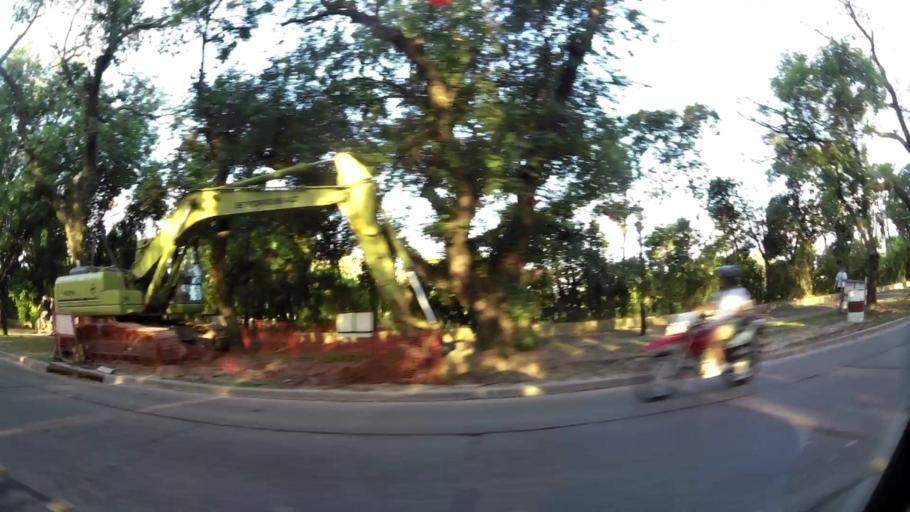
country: AR
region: Buenos Aires
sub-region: Partido de San Isidro
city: San Isidro
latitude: -34.4846
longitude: -58.5268
